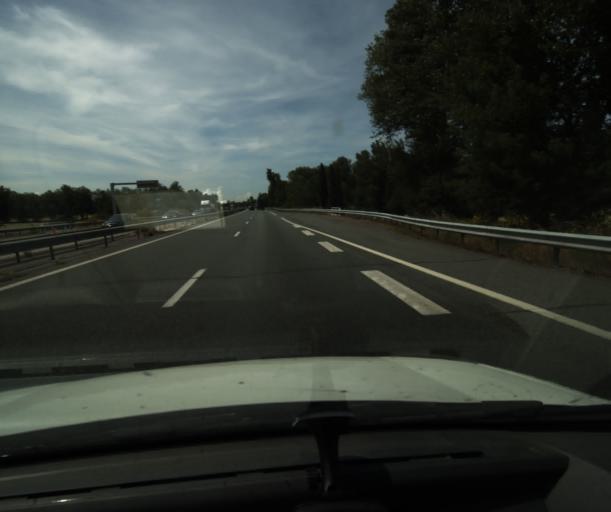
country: FR
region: Languedoc-Roussillon
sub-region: Departement de l'Aude
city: Saint-Martin-Lalande
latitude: 43.2800
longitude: 1.9852
